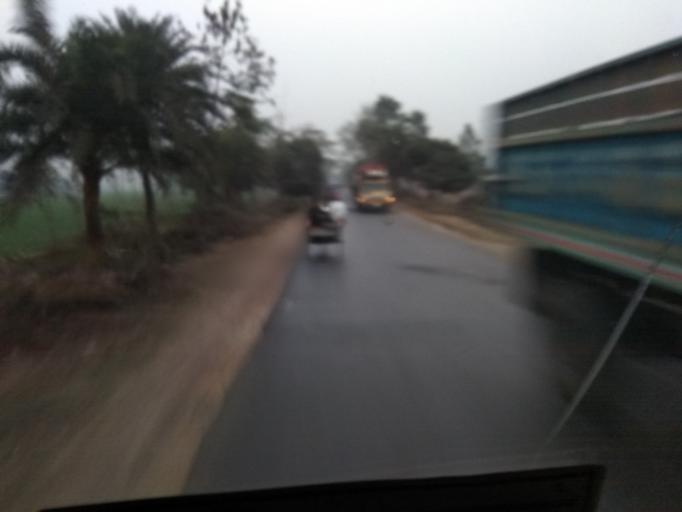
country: BD
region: Rajshahi
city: Bogra
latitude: 24.7425
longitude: 89.3348
